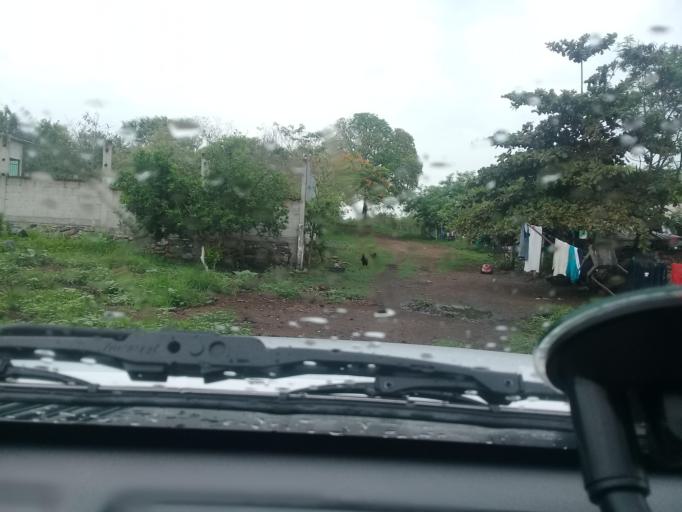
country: MX
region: Veracruz
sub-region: Puente Nacional
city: Cabezas
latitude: 19.3662
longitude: -96.3981
